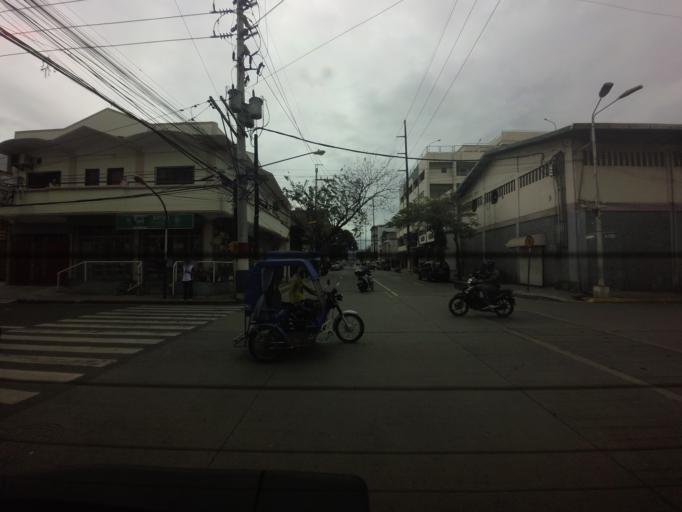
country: PH
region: Metro Manila
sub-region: City of Manila
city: Manila
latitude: 14.6279
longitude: 120.9695
